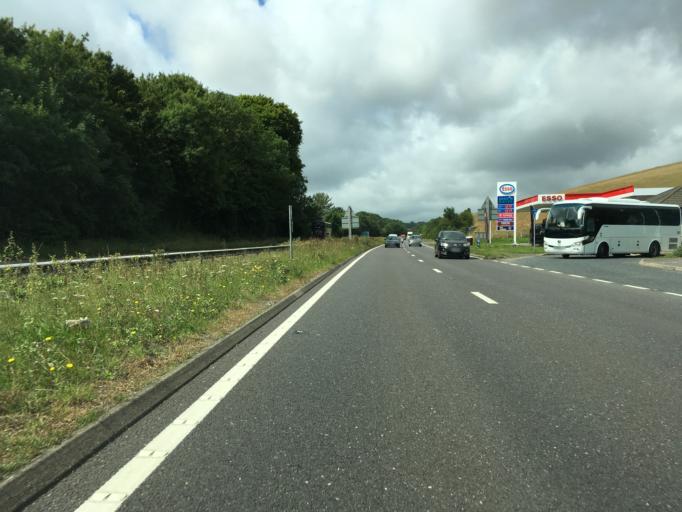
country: GB
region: England
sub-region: East Sussex
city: Lewes
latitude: 50.8654
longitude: -0.0459
